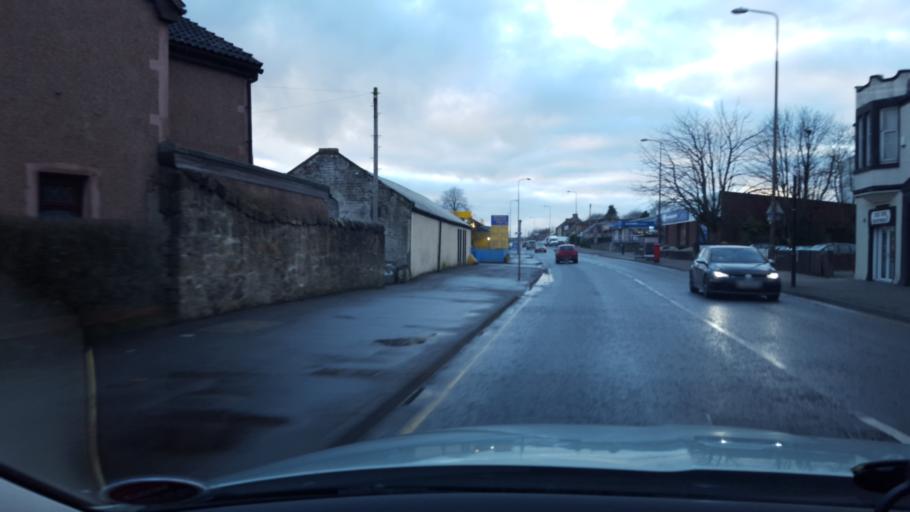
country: GB
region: Scotland
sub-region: West Lothian
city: Bathgate
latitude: 55.9017
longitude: -3.6485
